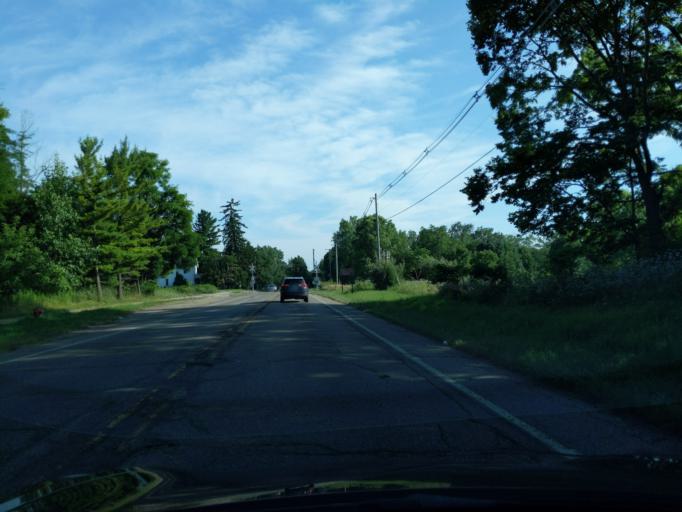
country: US
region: Michigan
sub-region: Ingham County
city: Okemos
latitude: 42.7354
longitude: -84.4276
